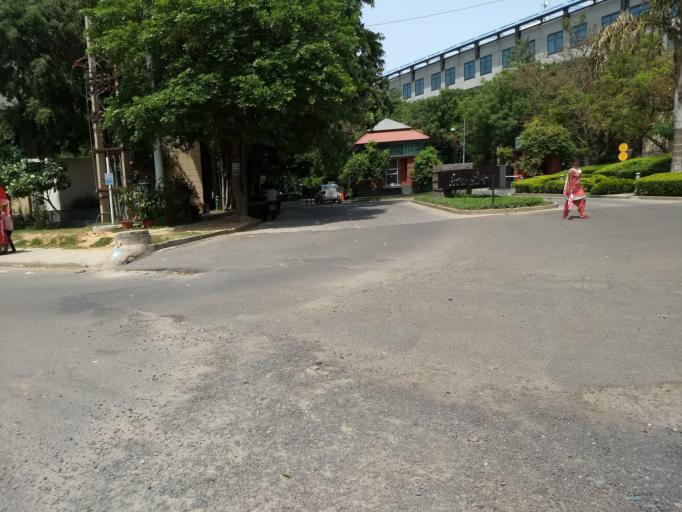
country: IN
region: Haryana
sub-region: Gurgaon
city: Gurgaon
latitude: 28.4580
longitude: 77.0971
